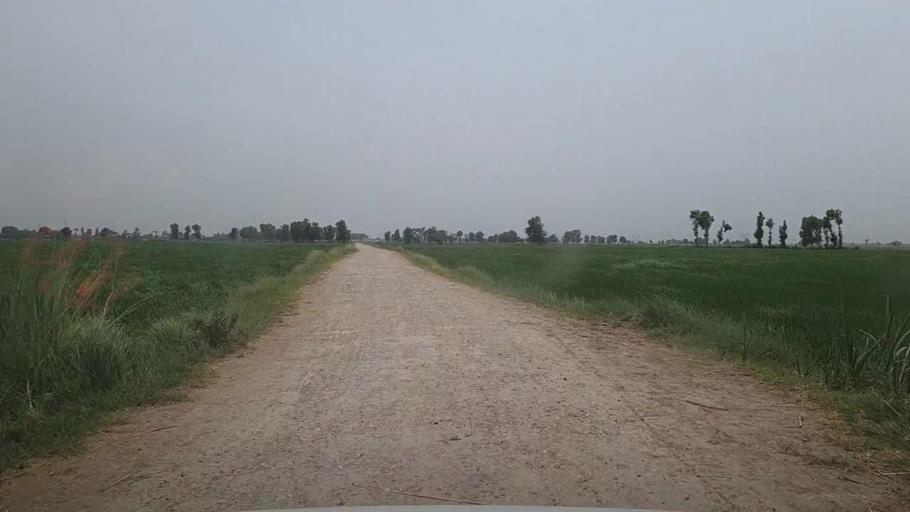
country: PK
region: Sindh
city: Sita Road
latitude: 27.0595
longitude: 67.8550
